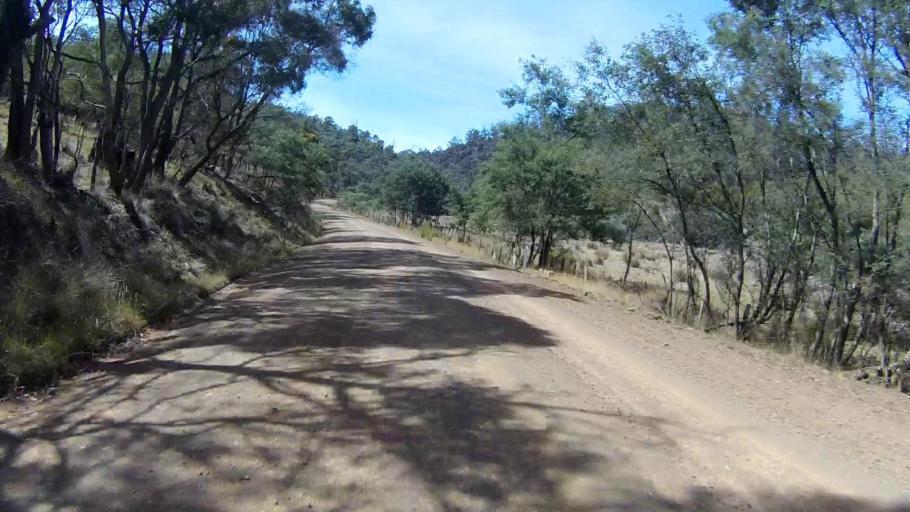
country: AU
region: Tasmania
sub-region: Sorell
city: Sorell
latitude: -42.6367
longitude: 147.7257
